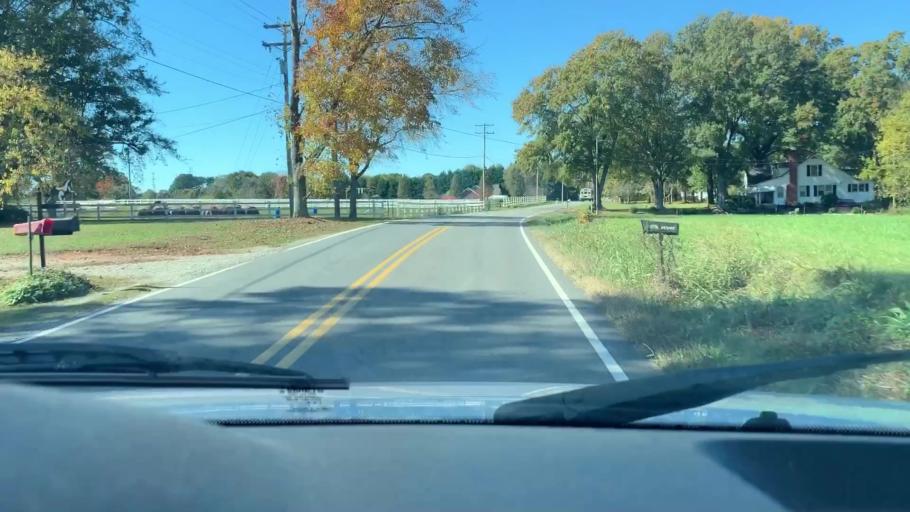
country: US
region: North Carolina
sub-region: Lincoln County
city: Westport
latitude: 35.4820
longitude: -80.9782
